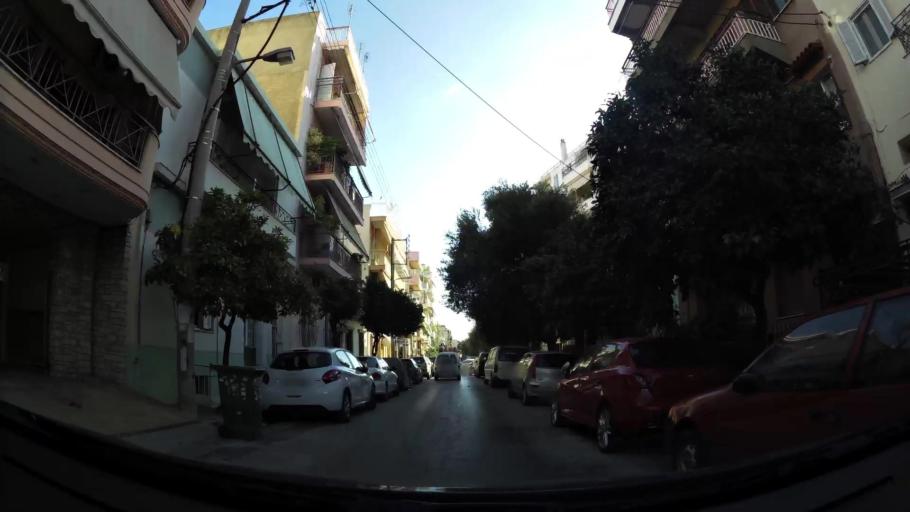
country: GR
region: Attica
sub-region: Nomos Piraios
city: Nikaia
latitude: 37.9729
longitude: 23.6565
